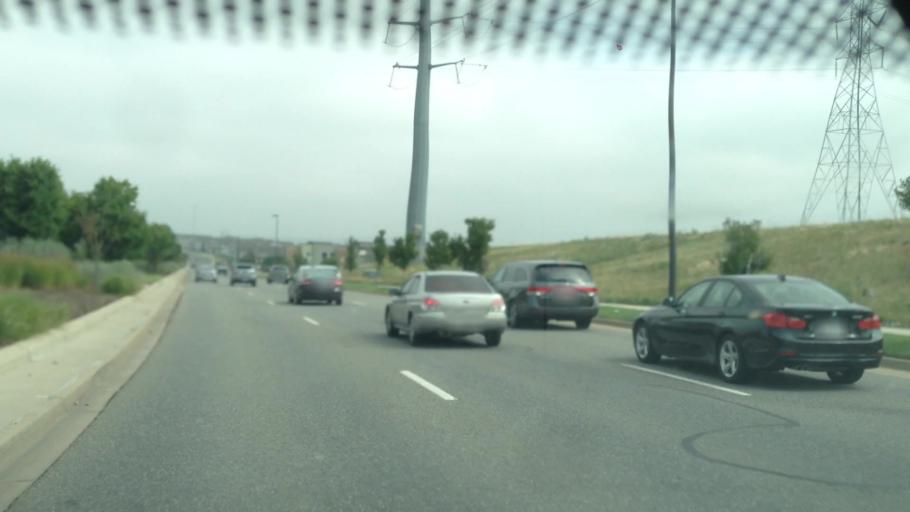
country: US
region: Colorado
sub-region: Douglas County
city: Parker
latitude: 39.6013
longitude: -104.7029
